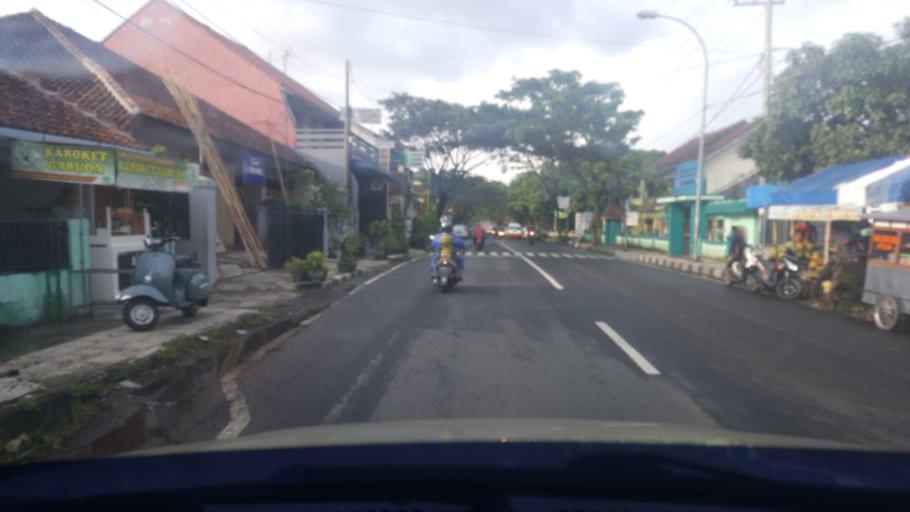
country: ID
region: West Java
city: Pakemitan
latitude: -7.2936
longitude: 108.2002
